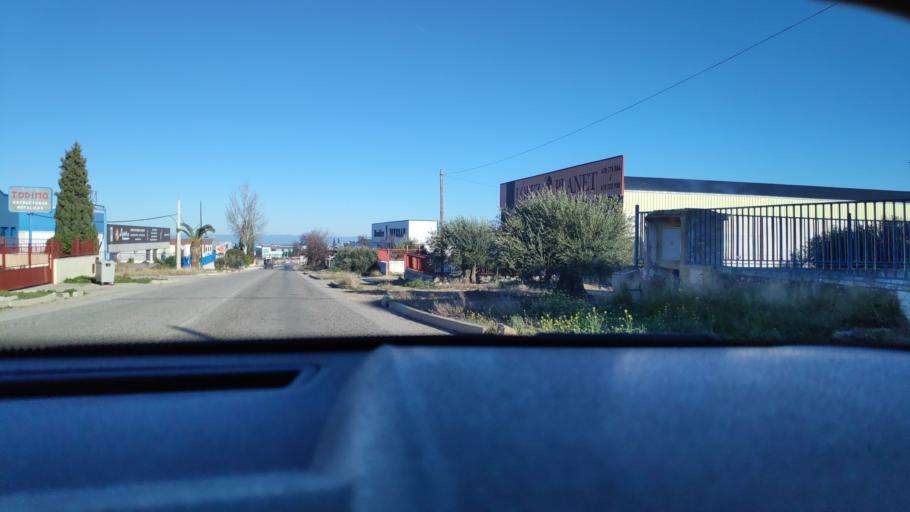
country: ES
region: Andalusia
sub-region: Provincia de Jaen
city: Mancha Real
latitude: 37.8029
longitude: -3.6107
